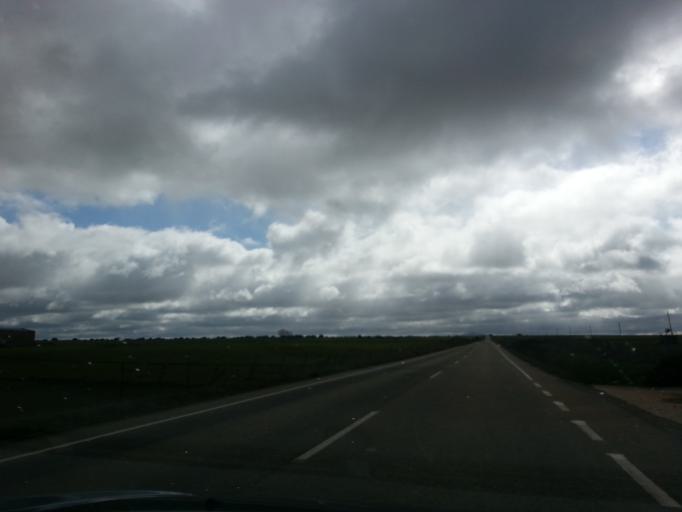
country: ES
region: Castille and Leon
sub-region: Provincia de Salamanca
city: La Fuente de San Esteban
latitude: 40.7734
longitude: -6.2260
